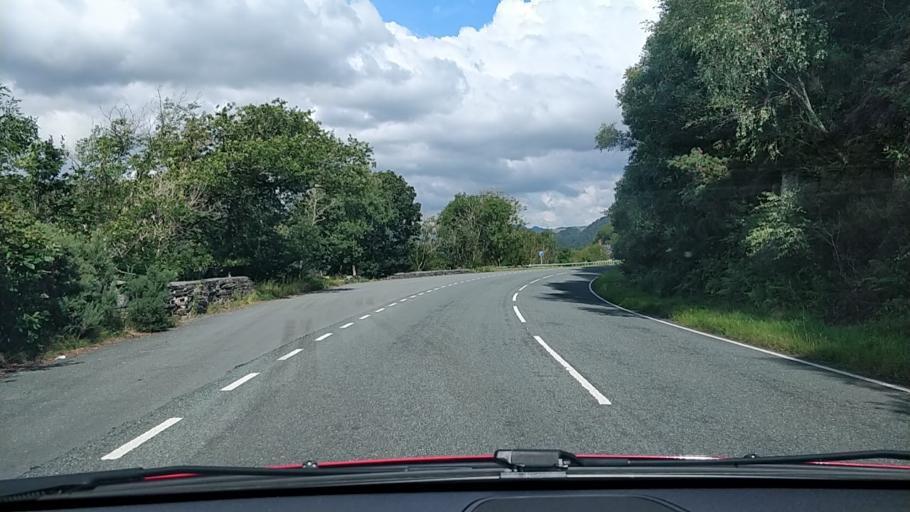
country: GB
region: Wales
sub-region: Gwynedd
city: Penrhyndeudraeth
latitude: 52.9360
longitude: -4.0309
